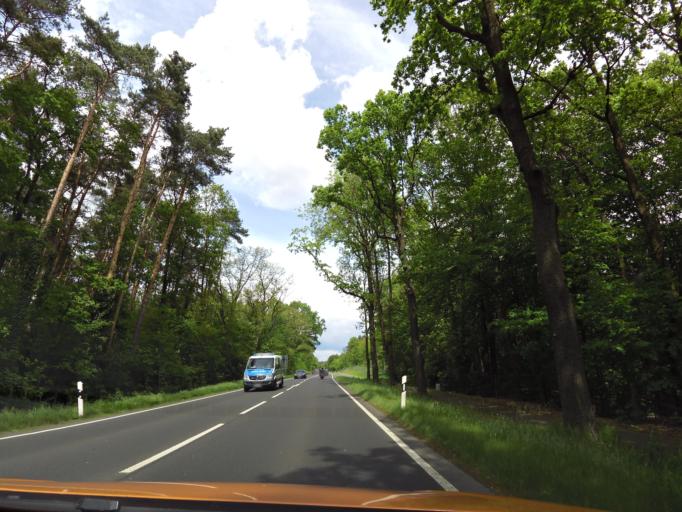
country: DE
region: Brandenburg
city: Michendorf
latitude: 52.2905
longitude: 13.0194
